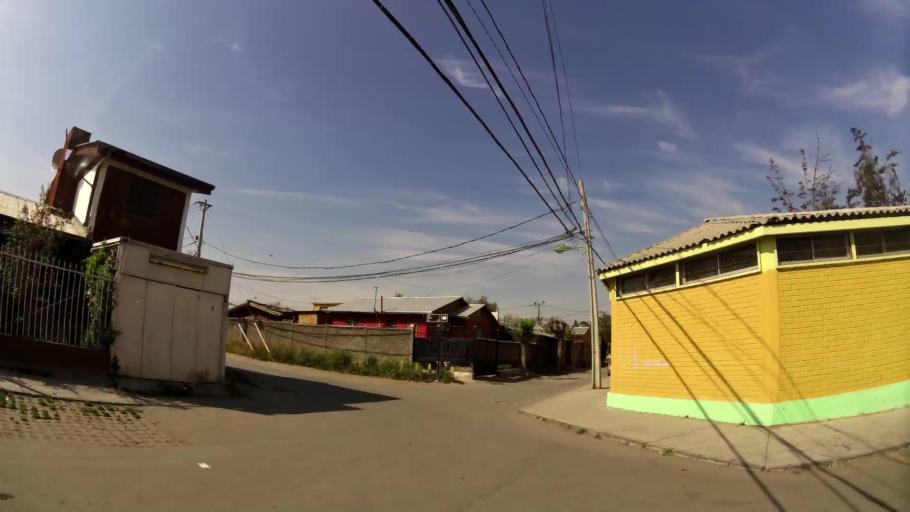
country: CL
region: Santiago Metropolitan
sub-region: Provincia de Santiago
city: La Pintana
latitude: -33.5593
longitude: -70.6694
